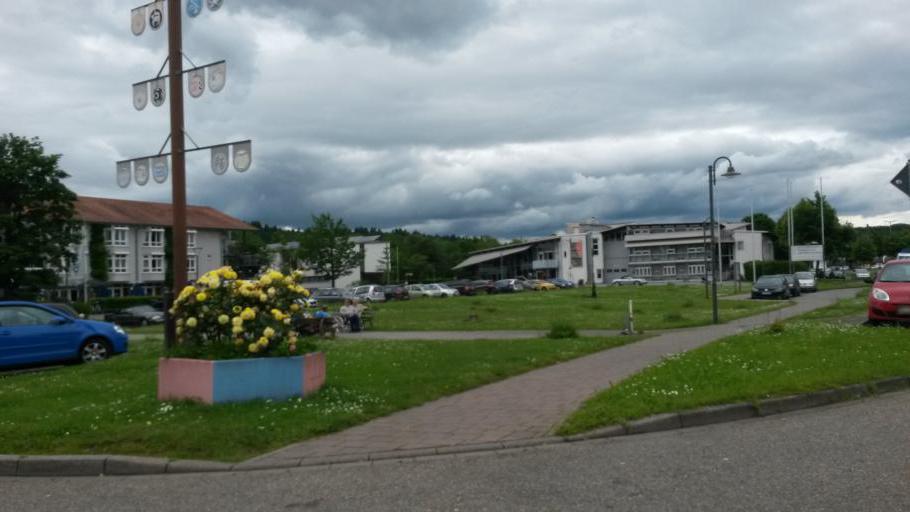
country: DE
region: Baden-Wuerttemberg
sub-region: Karlsruhe Region
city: Konigsbach-Stein
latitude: 48.9519
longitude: 8.5714
